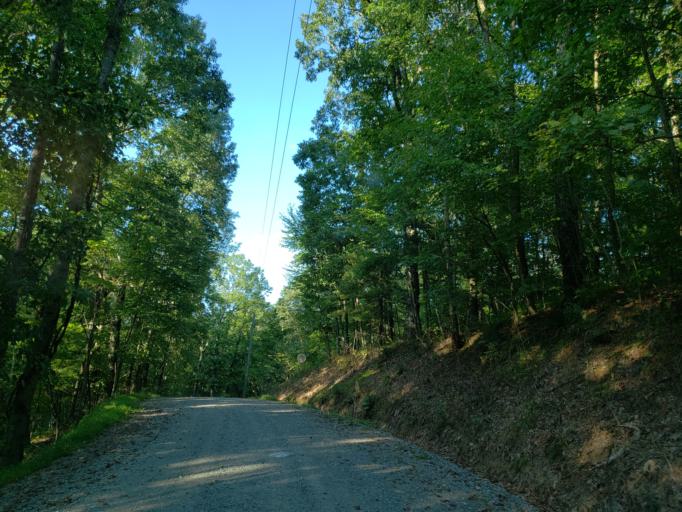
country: US
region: Georgia
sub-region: Fannin County
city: Blue Ridge
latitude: 34.6960
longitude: -84.2653
